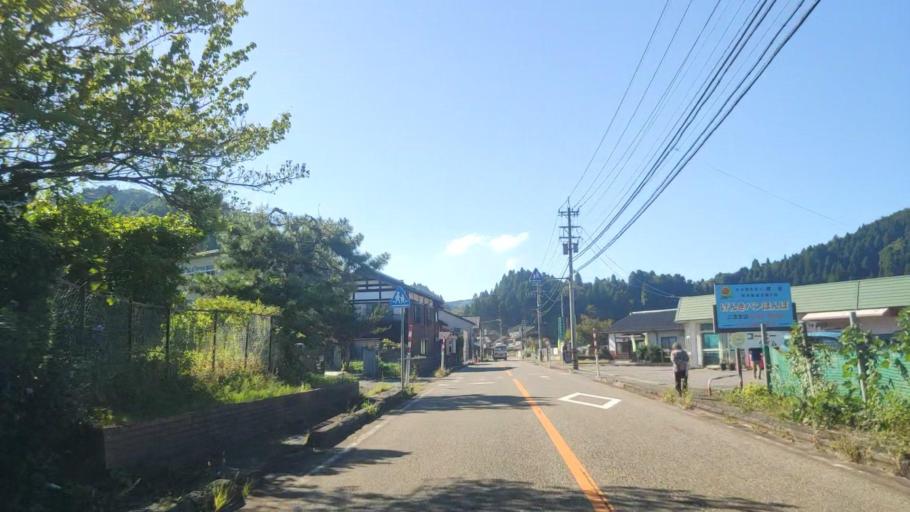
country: JP
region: Ishikawa
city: Nanao
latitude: 37.2814
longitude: 137.0421
